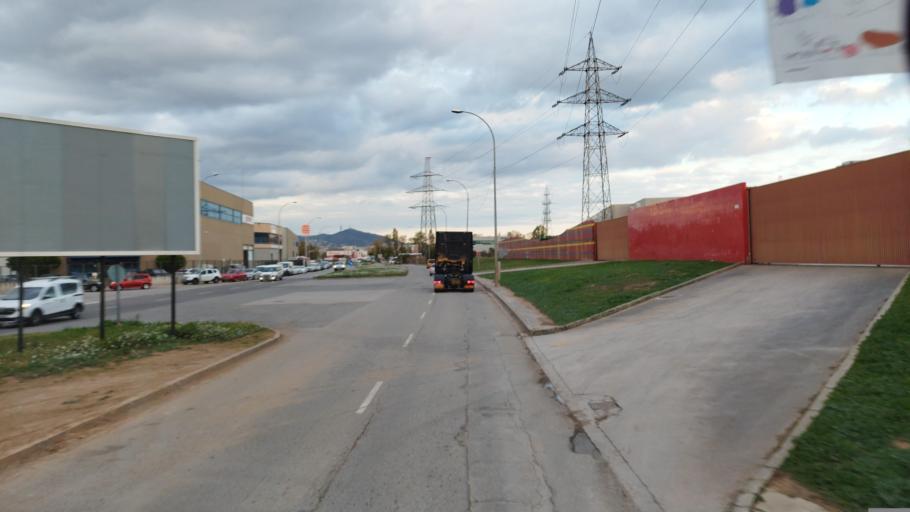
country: ES
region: Catalonia
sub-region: Provincia de Barcelona
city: Sant Boi de Llobregat
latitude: 41.3314
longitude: 2.0498
